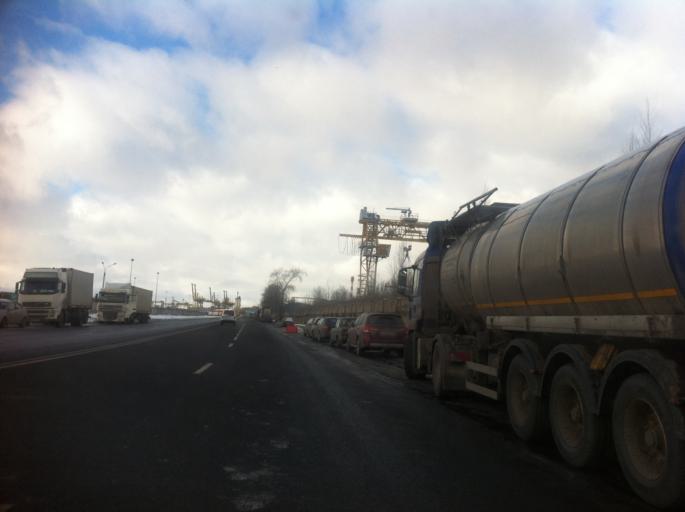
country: RU
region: St.-Petersburg
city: Avtovo
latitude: 59.8706
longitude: 30.2312
